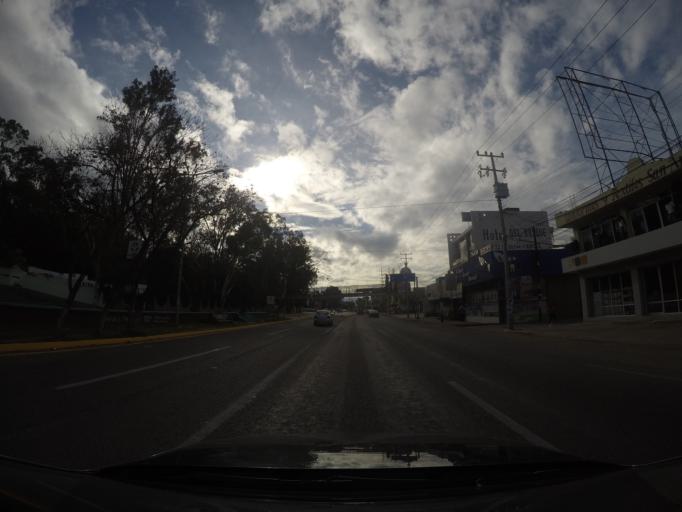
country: MX
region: Oaxaca
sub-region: Santa Cruz Amilpas
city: Santa Cruz Amilpas
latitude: 17.0690
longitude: -96.6979
